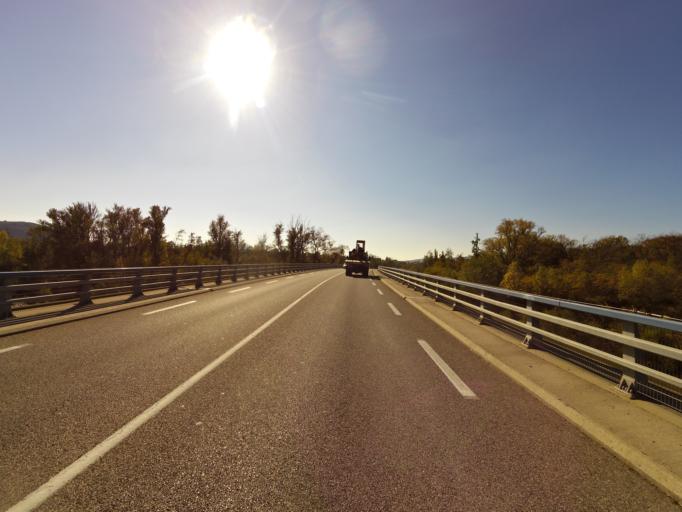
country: FR
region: Rhone-Alpes
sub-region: Departement de l'Ardeche
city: Saint-Privat
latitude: 44.6236
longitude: 4.4172
